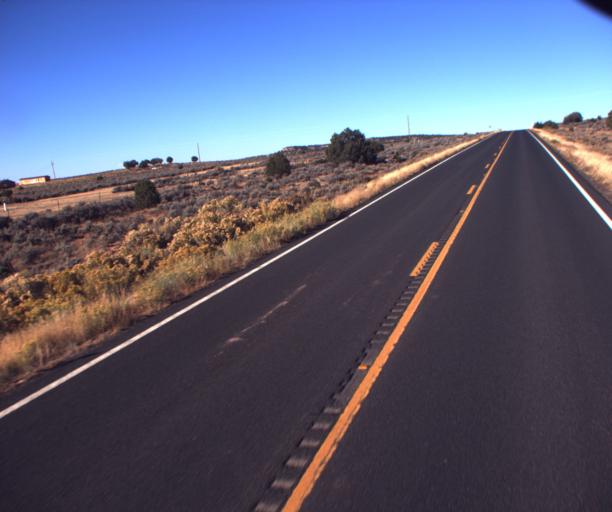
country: US
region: Arizona
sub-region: Apache County
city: Ganado
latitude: 35.7606
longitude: -109.7593
